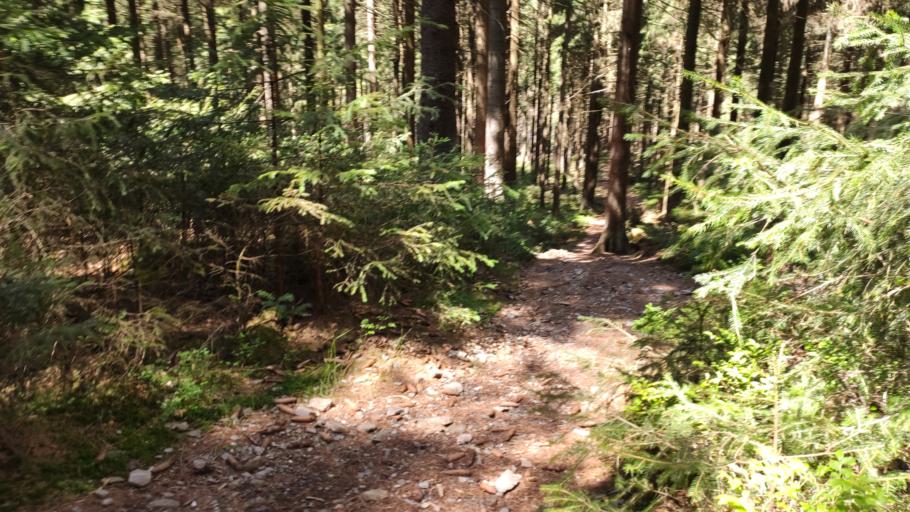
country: DE
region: Bavaria
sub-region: Upper Franconia
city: Reichenbach
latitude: 50.4504
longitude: 11.4533
